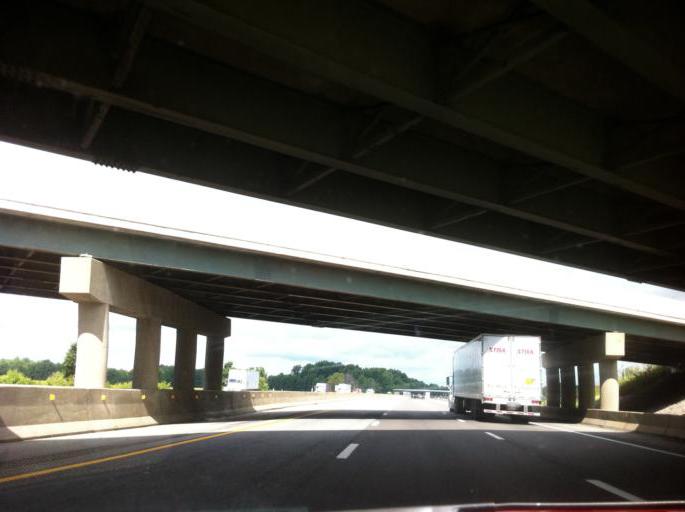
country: US
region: Ohio
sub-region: Trumbull County
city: Lordstown
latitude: 41.1469
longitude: -80.8859
